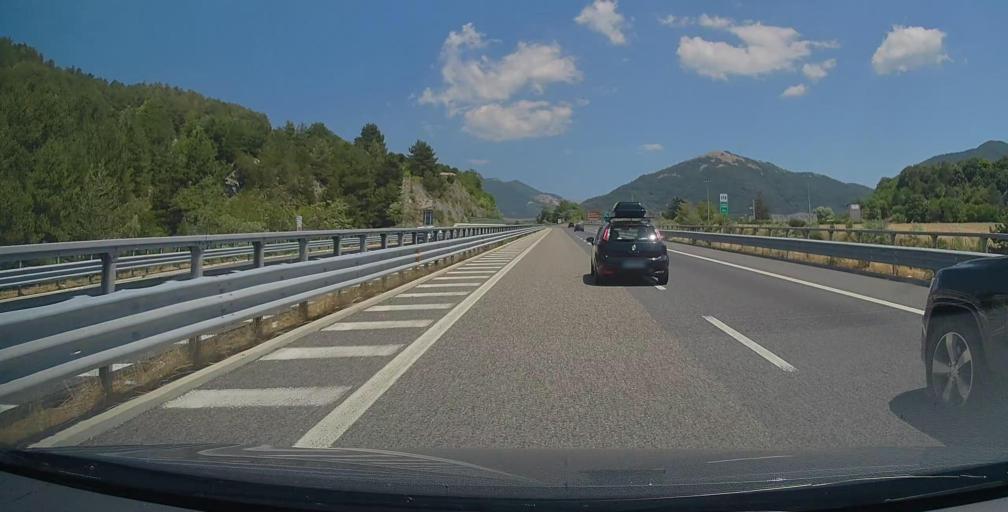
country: IT
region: Calabria
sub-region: Provincia di Cosenza
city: Mormanno
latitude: 39.8781
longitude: 16.0027
